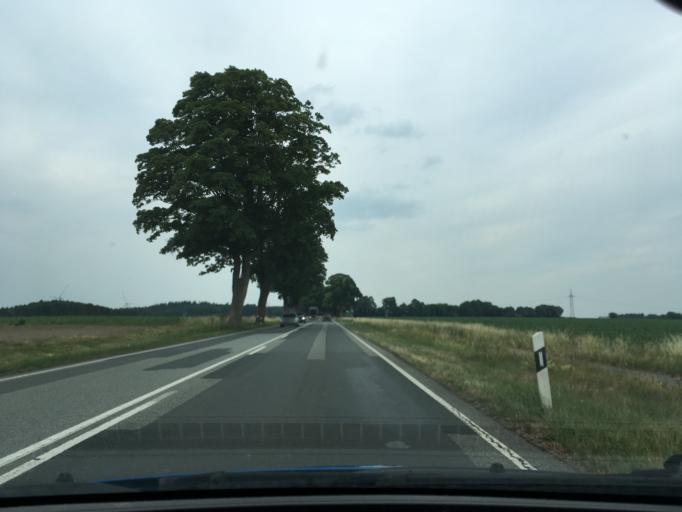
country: DE
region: Lower Saxony
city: Kakenstorf
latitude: 53.3147
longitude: 9.8058
